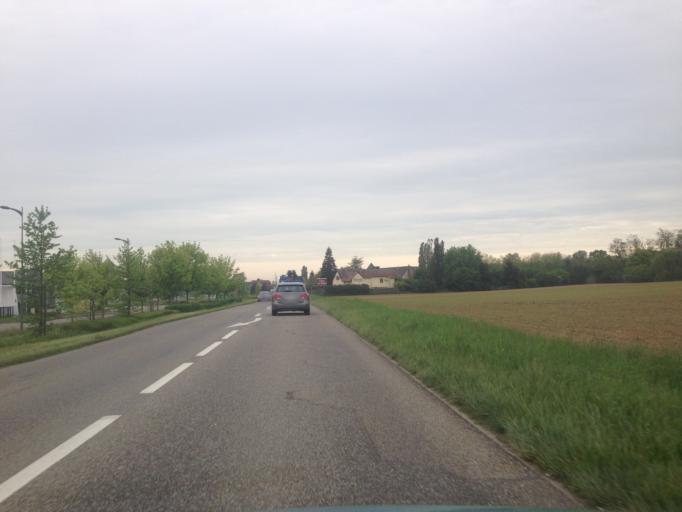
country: FR
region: Alsace
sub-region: Departement du Bas-Rhin
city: Mommenheim
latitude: 48.7530
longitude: 7.6614
